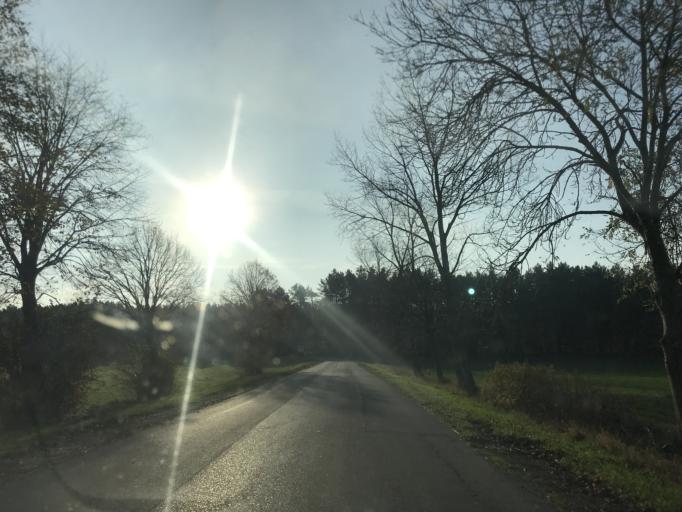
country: PL
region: Pomeranian Voivodeship
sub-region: Powiat pucki
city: Krokowa
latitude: 54.8054
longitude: 18.0993
